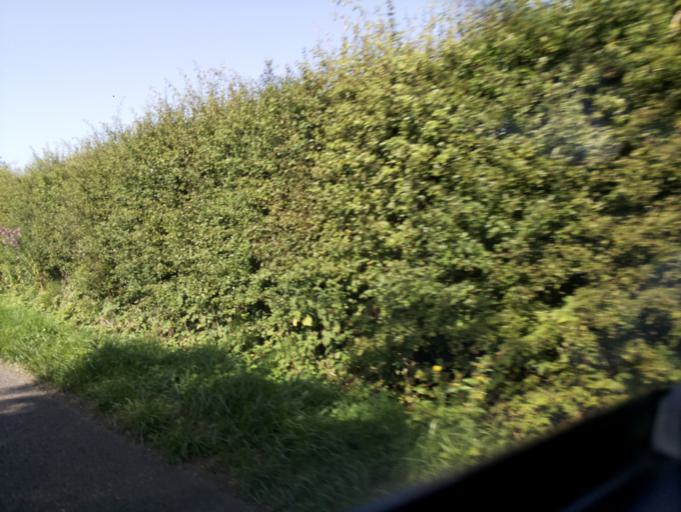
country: GB
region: England
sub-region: Oxfordshire
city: Ducklington
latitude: 51.7533
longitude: -1.4915
